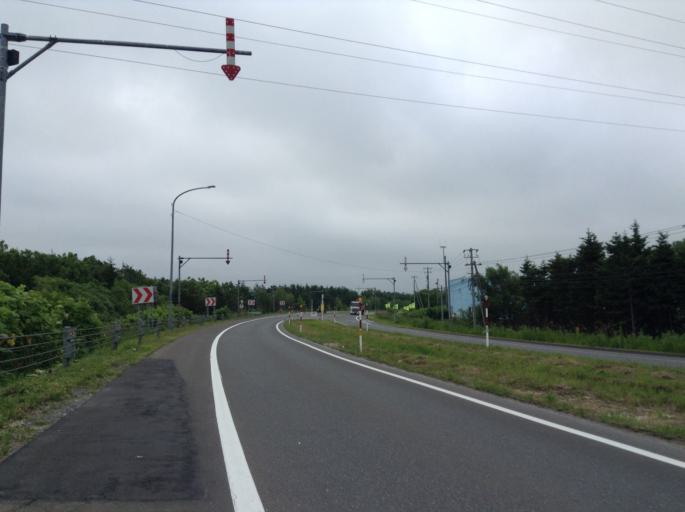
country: JP
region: Hokkaido
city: Wakkanai
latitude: 45.3691
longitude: 141.7263
